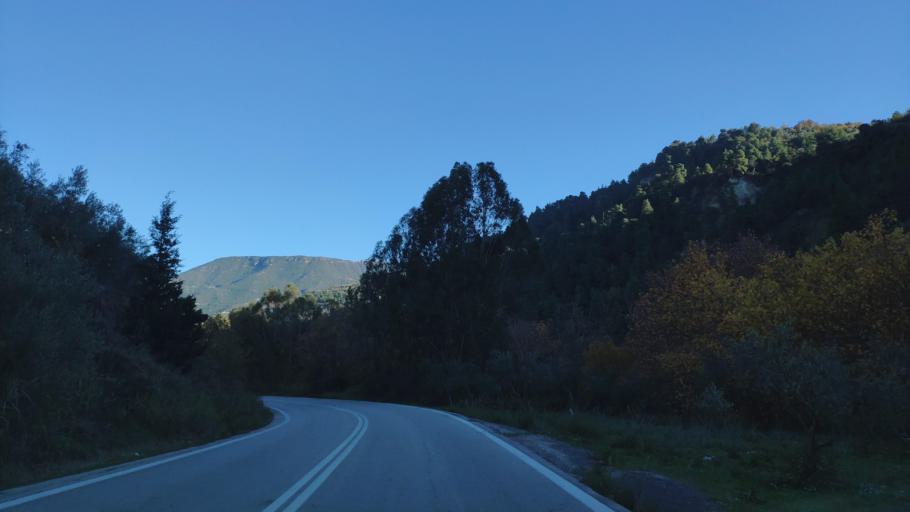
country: GR
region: Peloponnese
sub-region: Nomos Korinthias
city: Xylokastro
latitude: 38.0090
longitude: 22.5216
